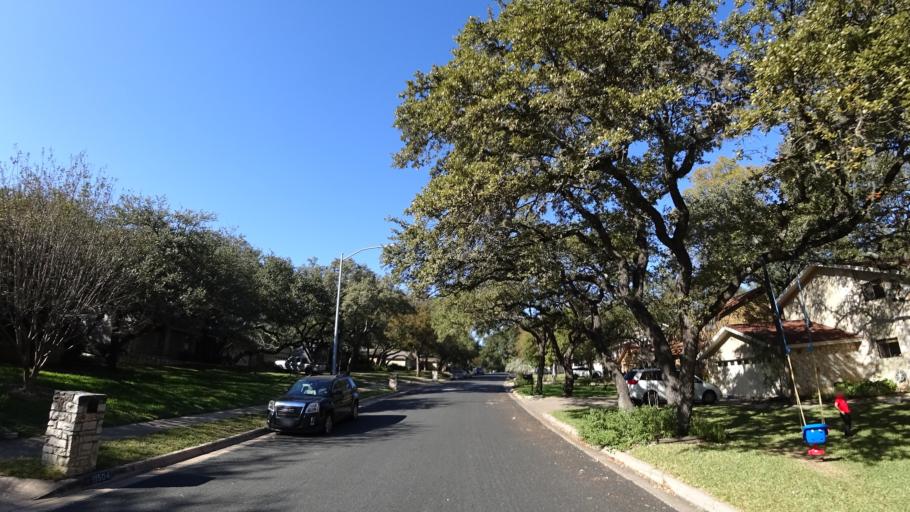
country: US
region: Texas
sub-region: Williamson County
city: Jollyville
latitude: 30.4248
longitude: -97.7698
